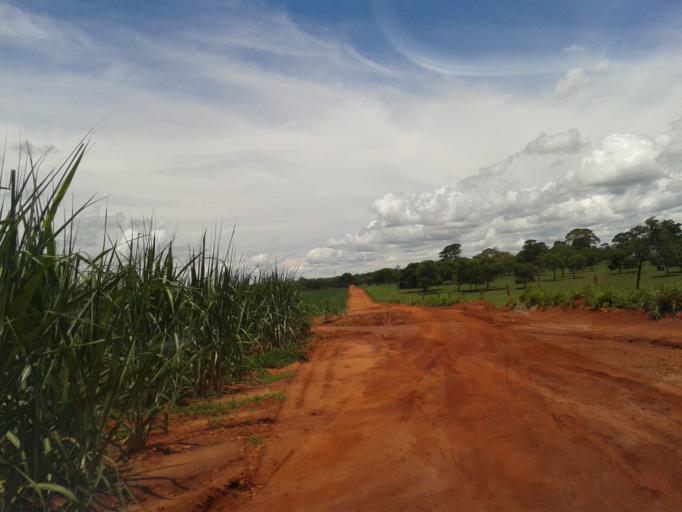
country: BR
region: Minas Gerais
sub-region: Santa Vitoria
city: Santa Vitoria
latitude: -19.2001
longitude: -50.6503
